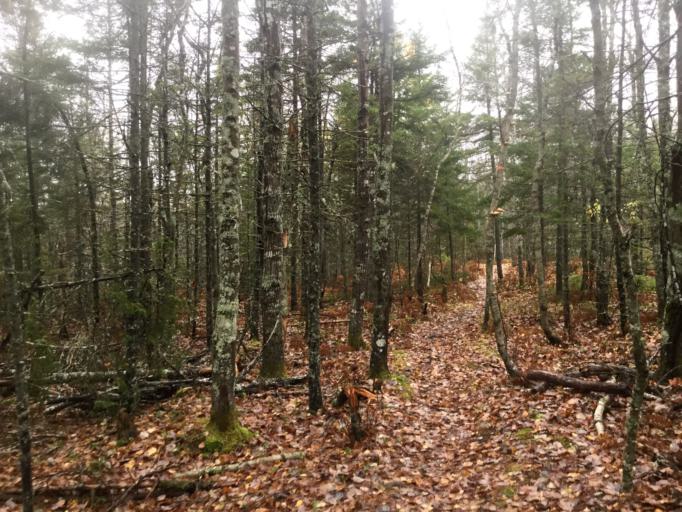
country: CA
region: Nova Scotia
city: New Glasgow
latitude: 45.5533
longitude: -62.6797
